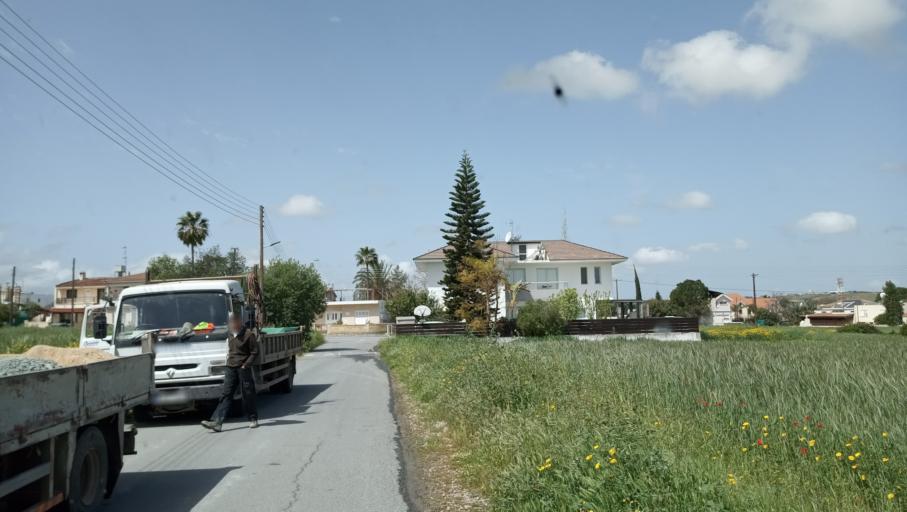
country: CY
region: Lefkosia
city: Dali
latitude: 35.0151
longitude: 33.4140
